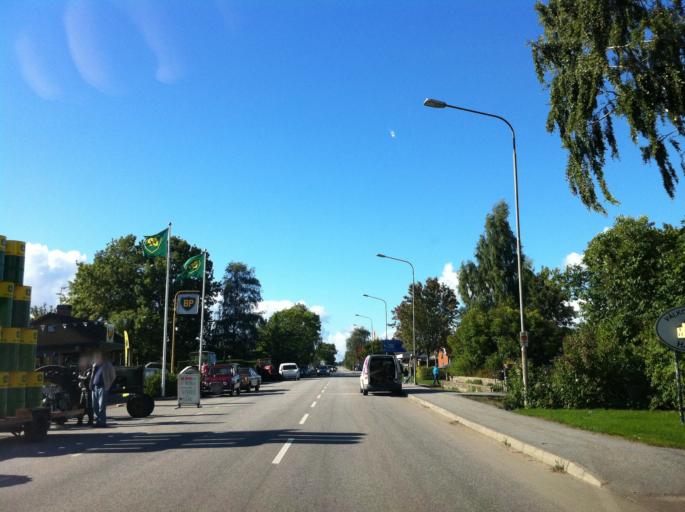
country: SE
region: Skane
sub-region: Hoors Kommun
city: Loberod
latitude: 55.7154
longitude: 13.5311
